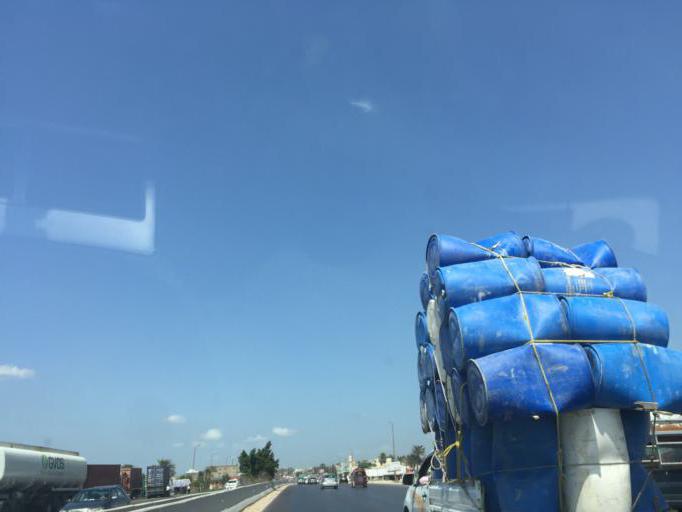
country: EG
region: Alexandria
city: Alexandria
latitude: 31.0675
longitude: 29.8212
